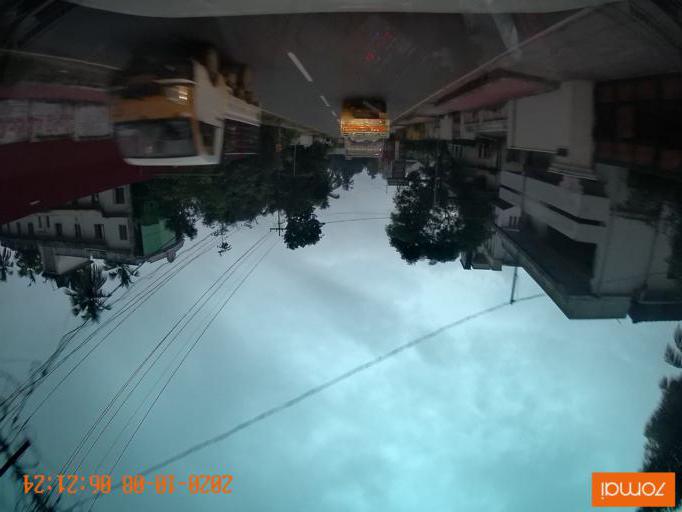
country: IN
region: Kerala
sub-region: Thrissur District
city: Trichur
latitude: 10.5206
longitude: 76.2319
